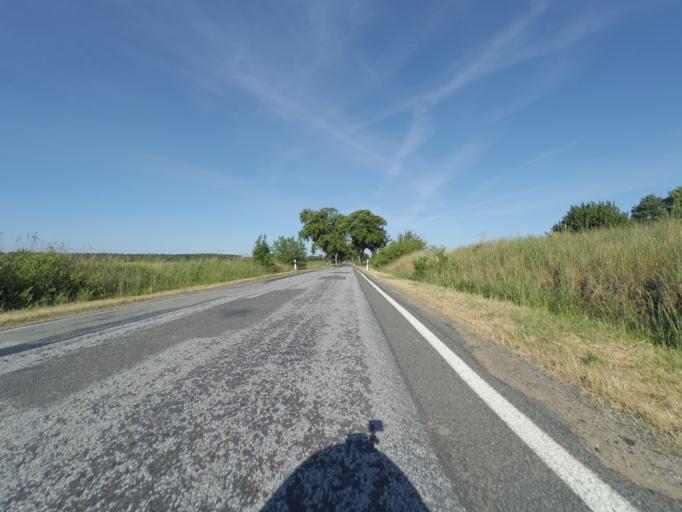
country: DE
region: Mecklenburg-Vorpommern
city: Plau am See
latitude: 53.3704
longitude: 12.1826
